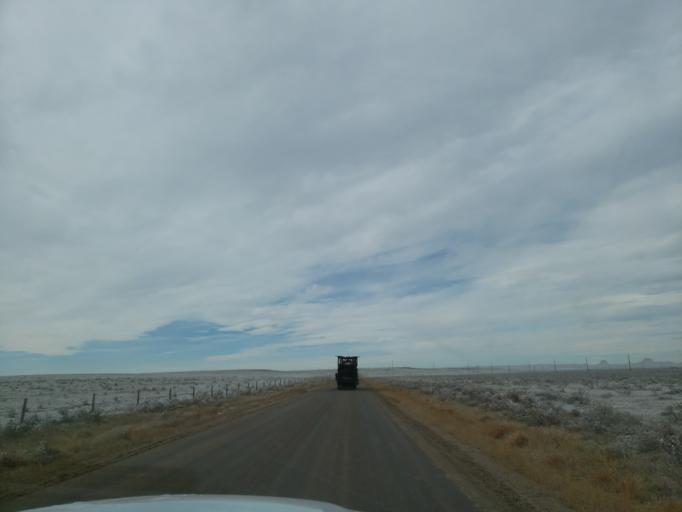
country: US
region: Wyoming
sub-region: Laramie County
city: Pine Bluffs
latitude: 40.7877
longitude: -103.8793
